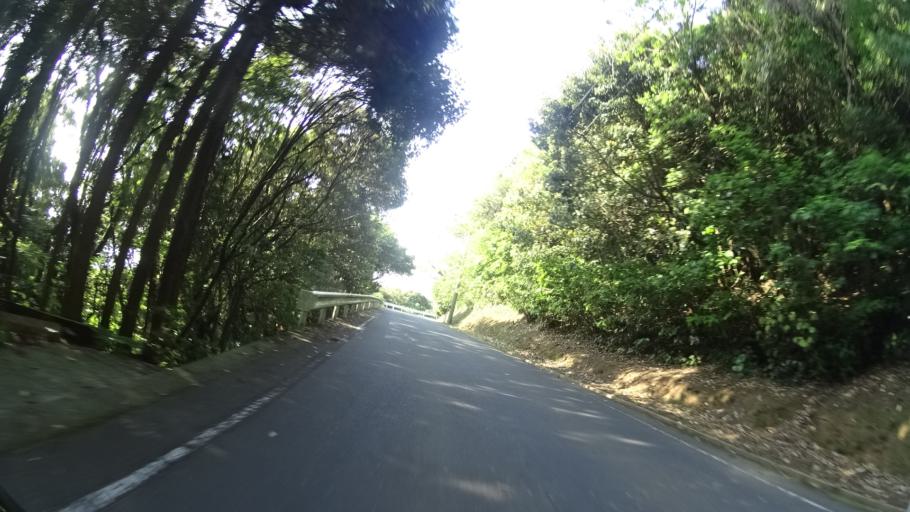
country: JP
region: Ehime
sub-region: Nishiuwa-gun
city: Ikata-cho
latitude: 33.3749
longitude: 132.0618
